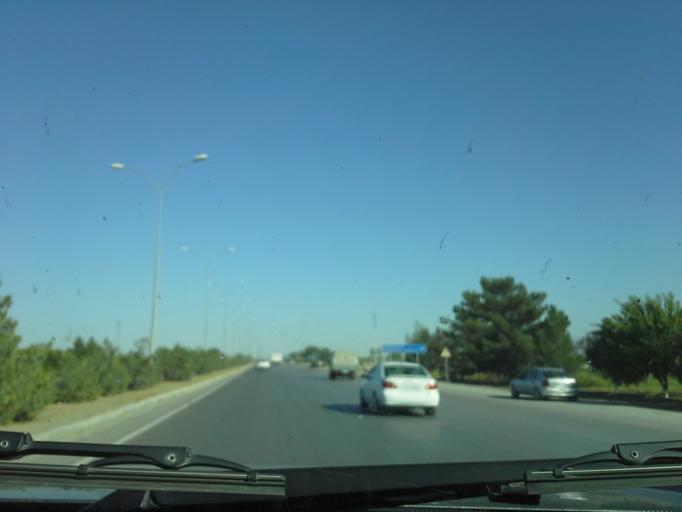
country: TM
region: Ahal
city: Abadan
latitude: 38.1218
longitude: 58.0401
